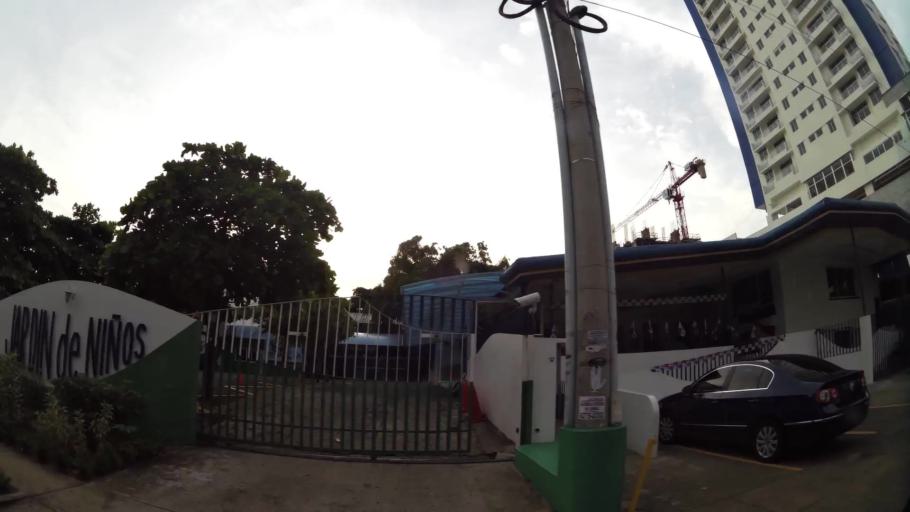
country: PA
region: Panama
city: Panama
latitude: 8.9937
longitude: -79.5069
